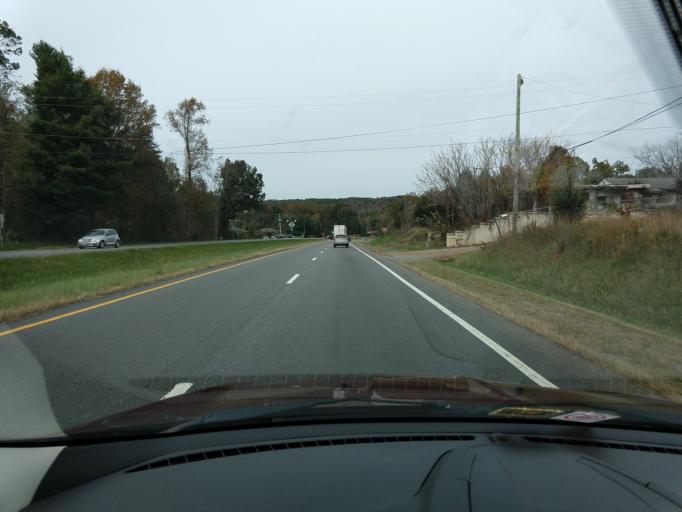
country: US
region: Virginia
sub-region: Franklin County
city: Rocky Mount
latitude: 37.0473
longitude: -79.8795
